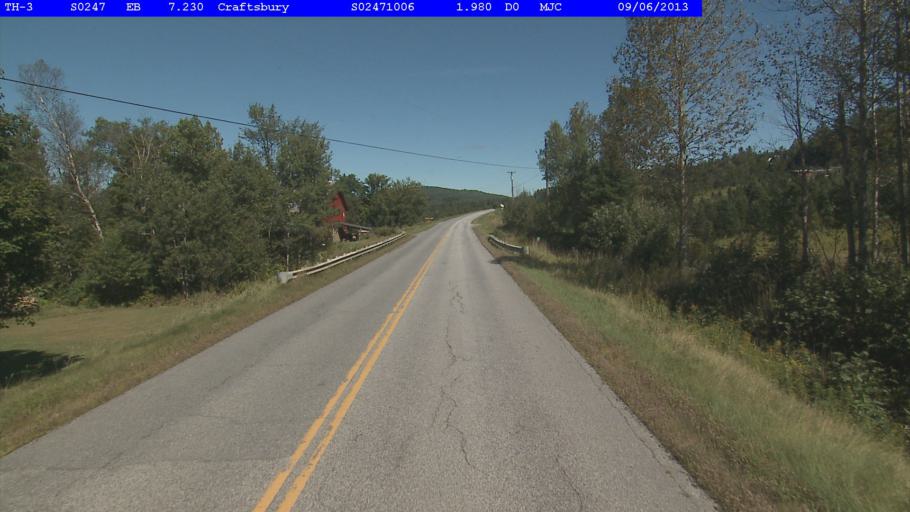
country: US
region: Vermont
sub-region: Caledonia County
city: Hardwick
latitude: 44.6399
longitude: -72.4193
